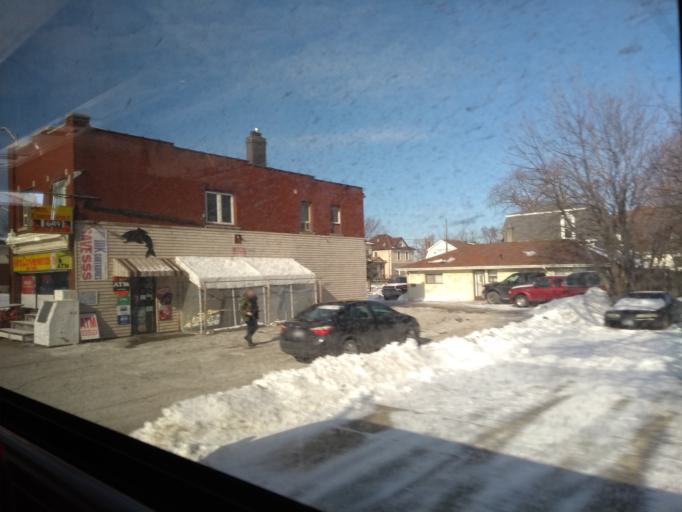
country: CA
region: Ontario
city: Niagara Falls
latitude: 43.1087
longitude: -79.0784
